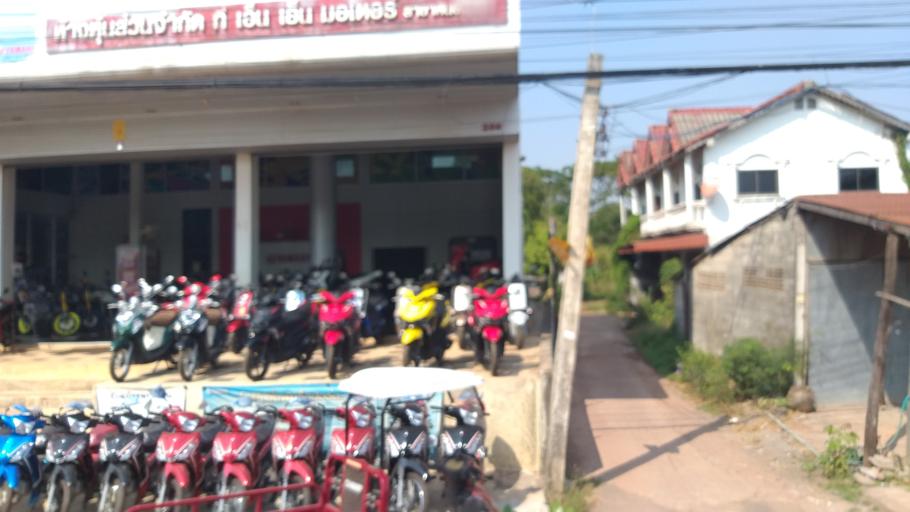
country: TH
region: Changwat Udon Thani
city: Nong Han
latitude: 17.3634
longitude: 103.1125
